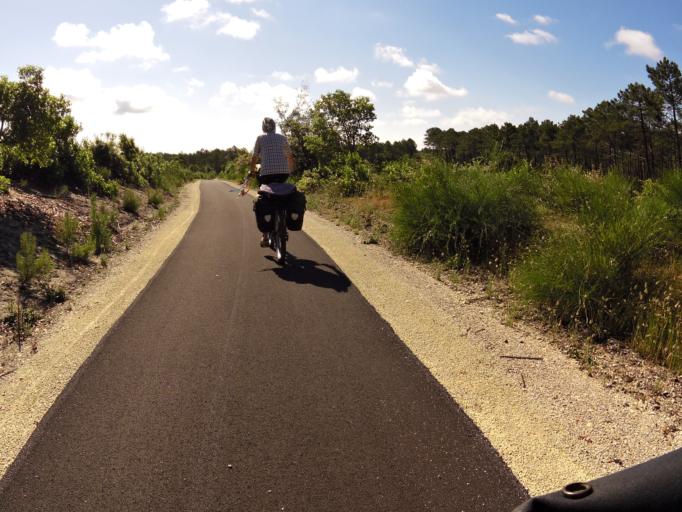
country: FR
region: Aquitaine
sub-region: Departement de la Gironde
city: Lacanau
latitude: 45.0330
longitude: -1.1796
